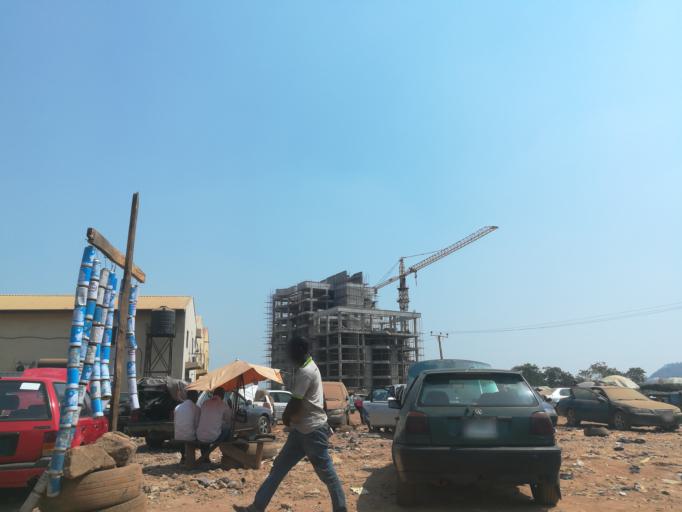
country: NG
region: Abuja Federal Capital Territory
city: Abuja
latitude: 9.0626
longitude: 7.4324
